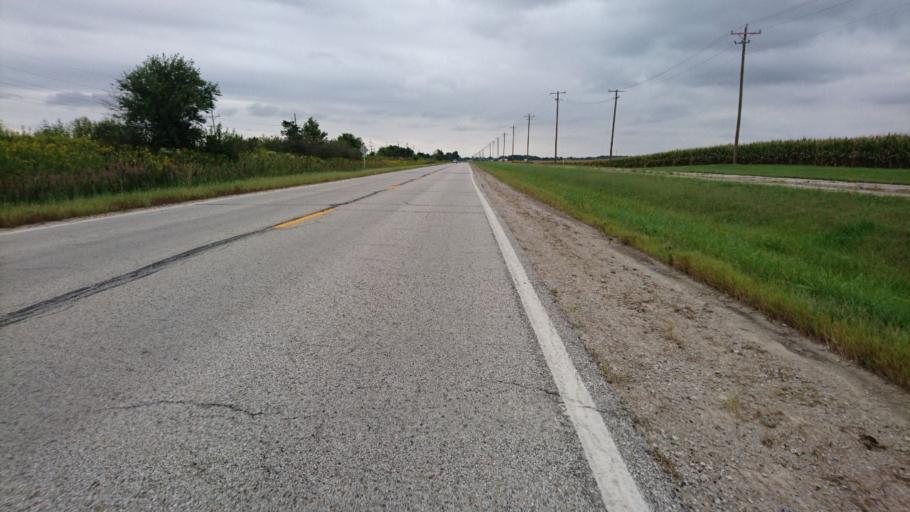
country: US
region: Illinois
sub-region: Livingston County
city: Pontiac
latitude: 40.9160
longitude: -88.6067
